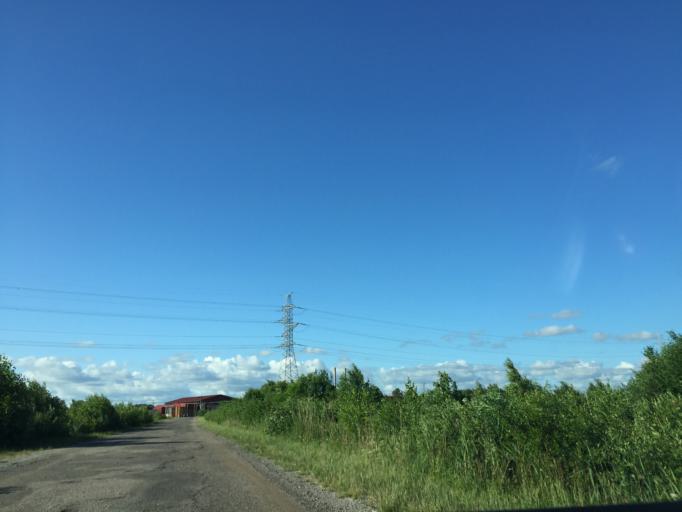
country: LV
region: Ventspils
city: Ventspils
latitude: 57.3997
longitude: 21.6491
